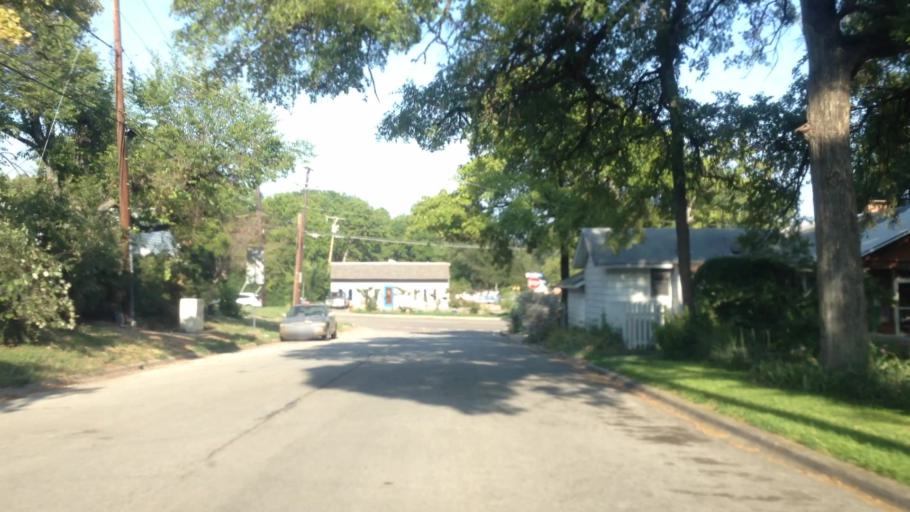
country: US
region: Texas
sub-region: Tarrant County
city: Haltom City
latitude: 32.7999
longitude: -97.2566
